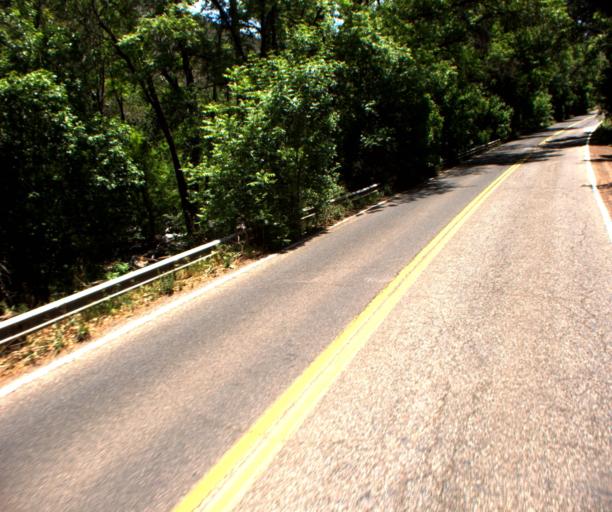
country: US
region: Arizona
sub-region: Coconino County
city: Sedona
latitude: 34.9056
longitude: -111.7277
